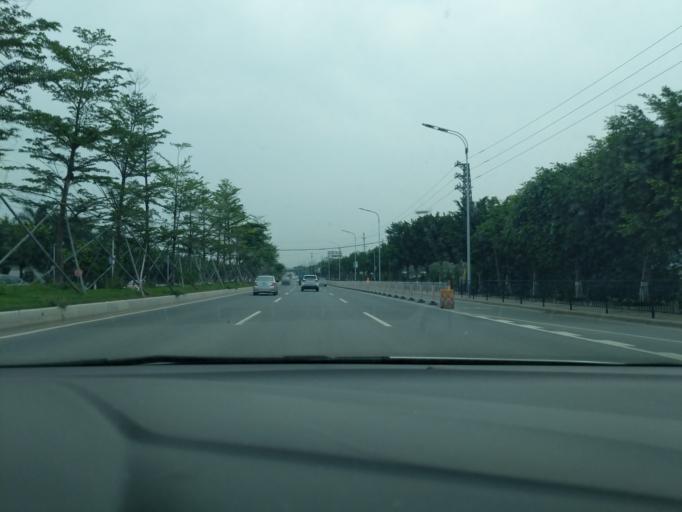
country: CN
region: Guangdong
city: Dongyong
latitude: 22.8624
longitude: 113.4834
